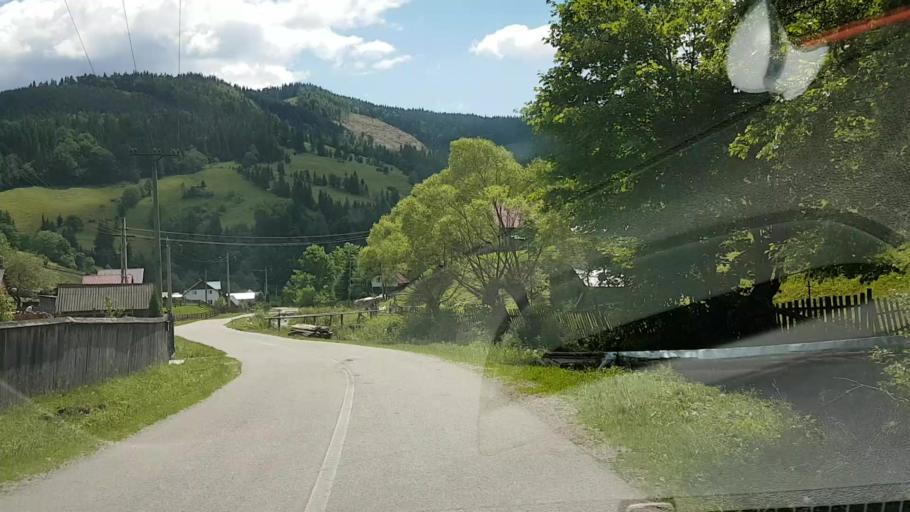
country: RO
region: Suceava
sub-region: Comuna Crucea
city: Crucea
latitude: 47.4190
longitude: 25.5811
